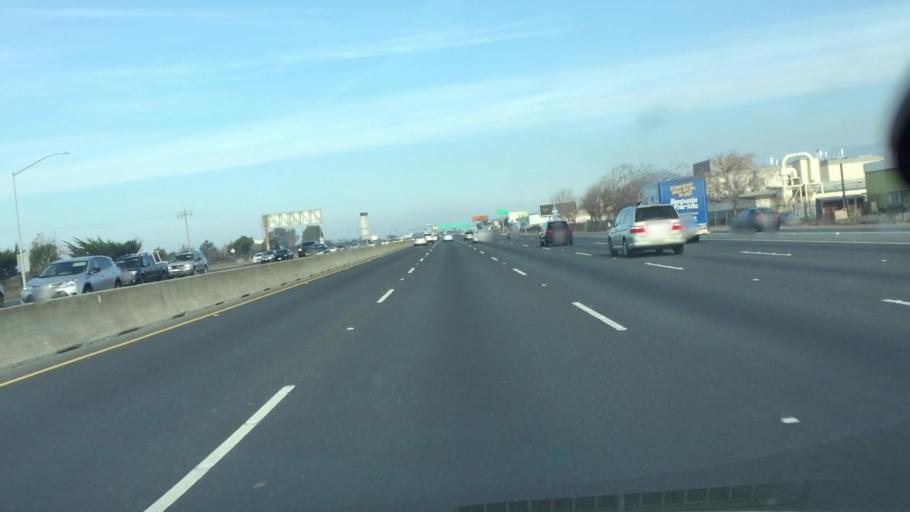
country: US
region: California
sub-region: Alameda County
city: Albany
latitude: 37.8684
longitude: -122.3042
